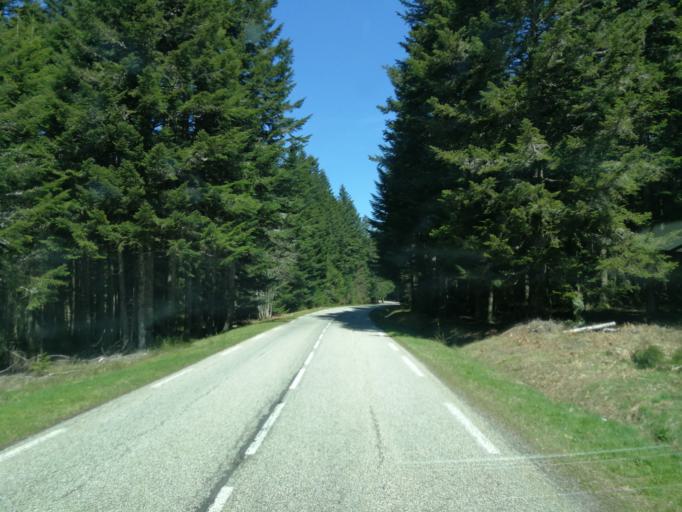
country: FR
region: Rhone-Alpes
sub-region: Departement de l'Ardeche
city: Saint-Agreve
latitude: 45.1076
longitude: 4.4048
